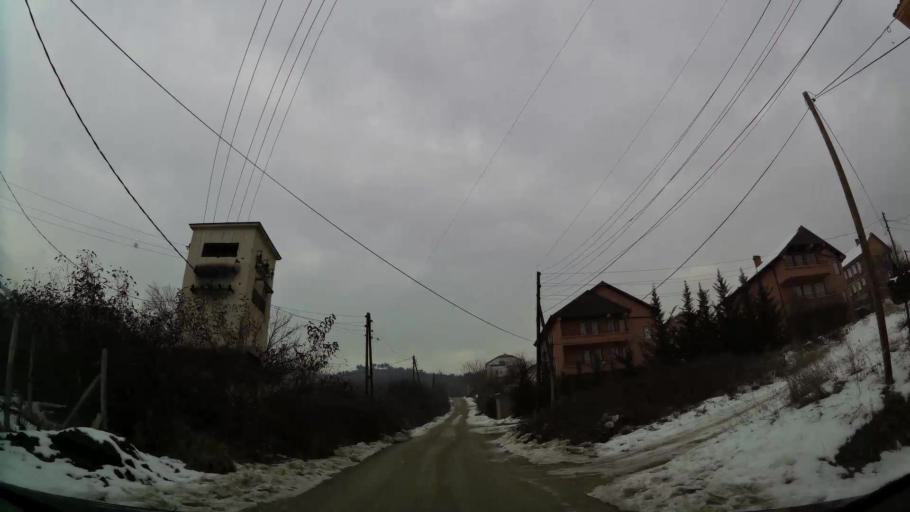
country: MK
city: Kondovo
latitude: 42.0138
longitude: 21.3066
